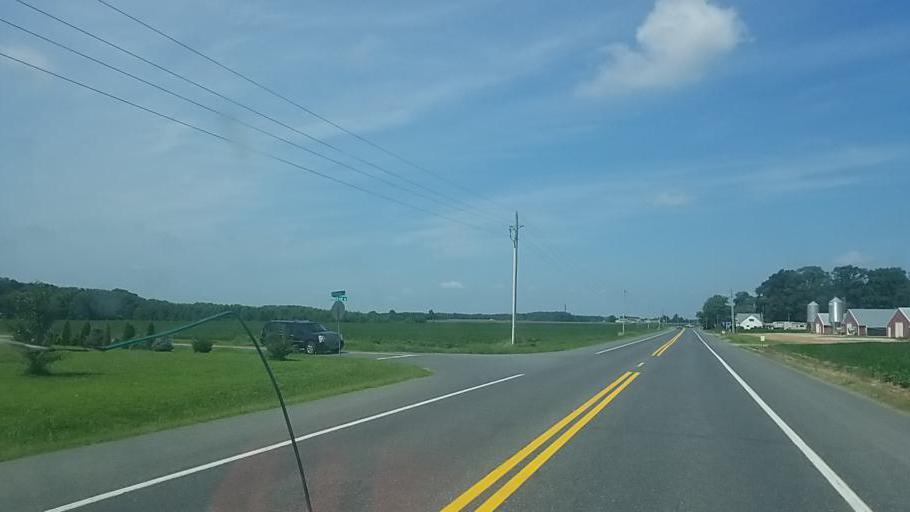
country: US
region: Delaware
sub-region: Sussex County
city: Bridgeville
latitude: 38.8253
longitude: -75.6487
